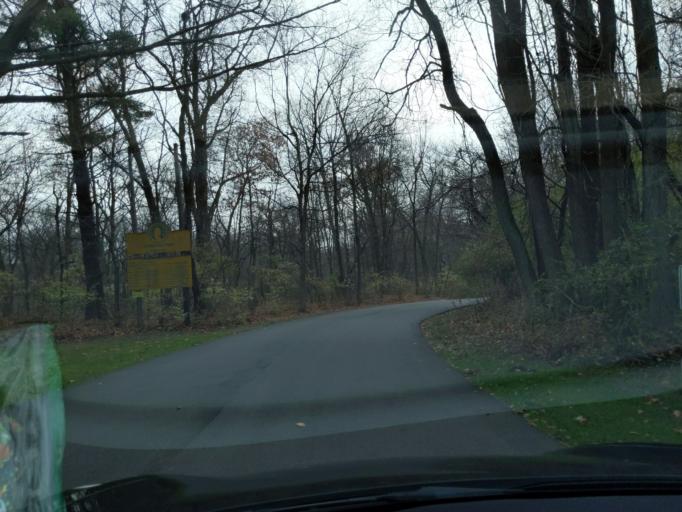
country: US
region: Indiana
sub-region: Saint Joseph County
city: Georgetown
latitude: 41.7299
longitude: -86.2633
